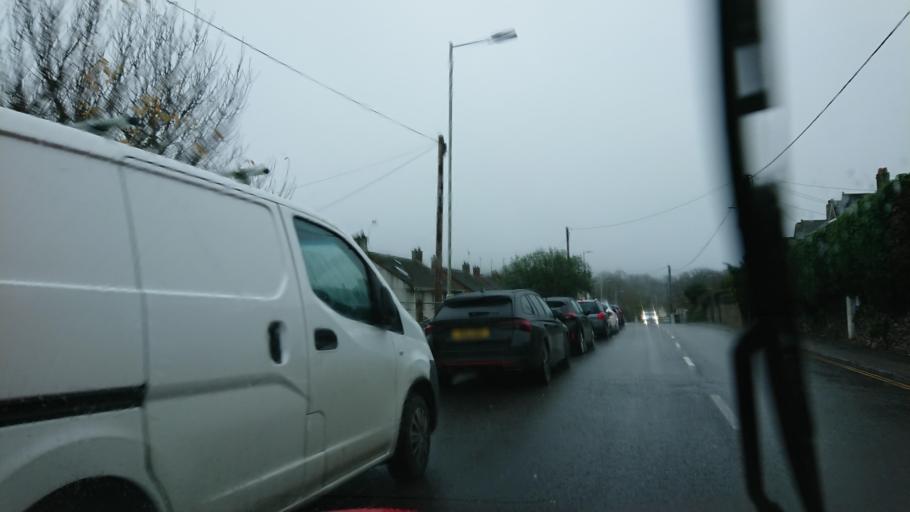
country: GB
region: England
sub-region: Plymouth
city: Plymstock
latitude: 50.3586
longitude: -4.0967
